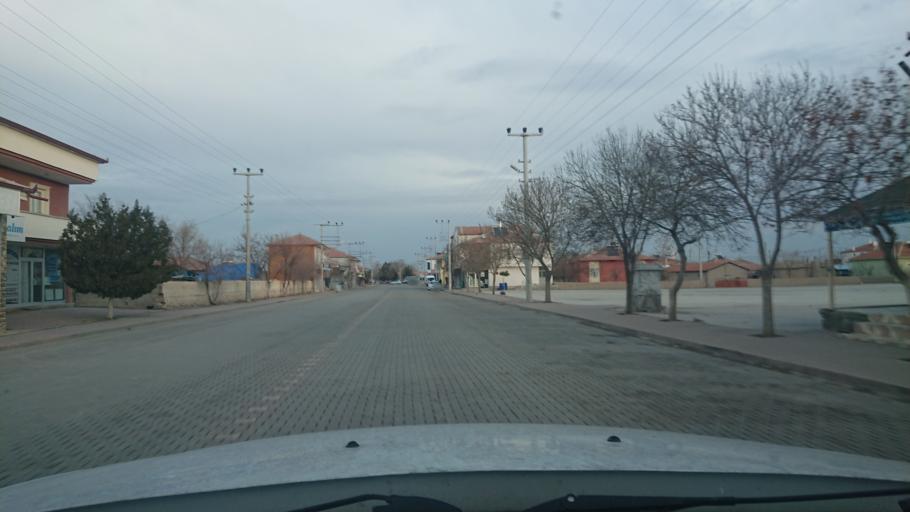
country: TR
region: Aksaray
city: Yesilova
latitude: 38.3408
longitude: 33.7503
